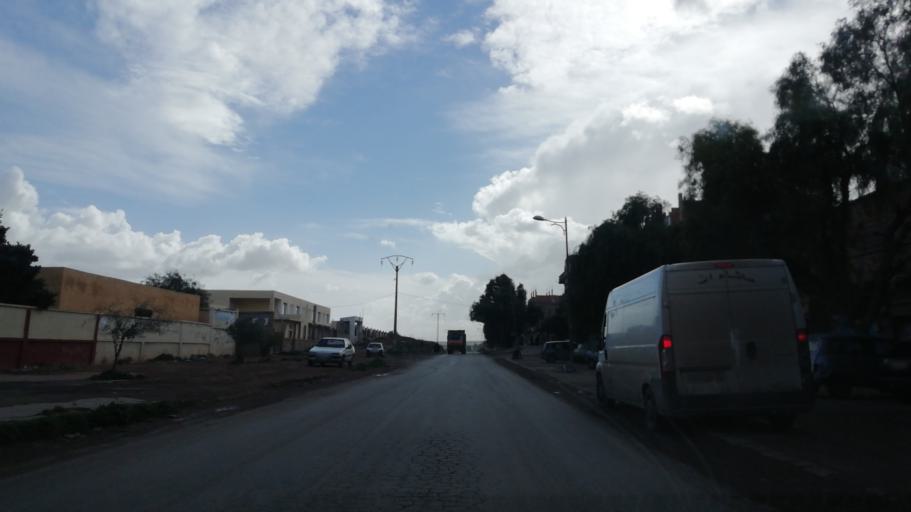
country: DZ
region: Oran
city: Sidi ech Chahmi
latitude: 35.6486
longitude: -0.5625
